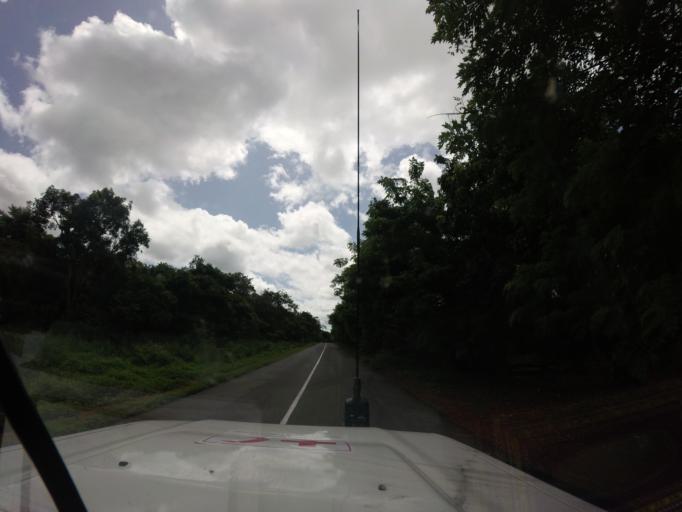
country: SL
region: Northern Province
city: Bindi
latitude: 10.1590
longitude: -11.6942
